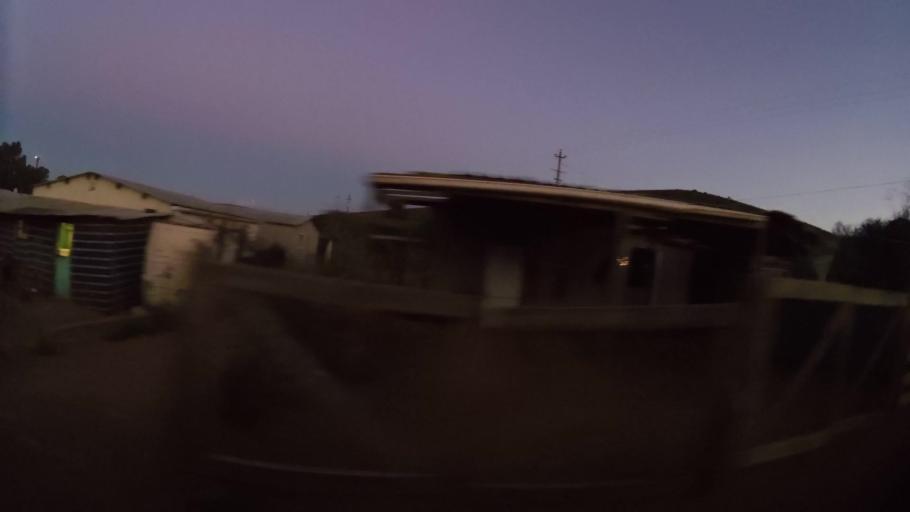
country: ZA
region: Western Cape
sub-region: Eden District Municipality
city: Riversdale
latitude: -34.1066
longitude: 21.2742
